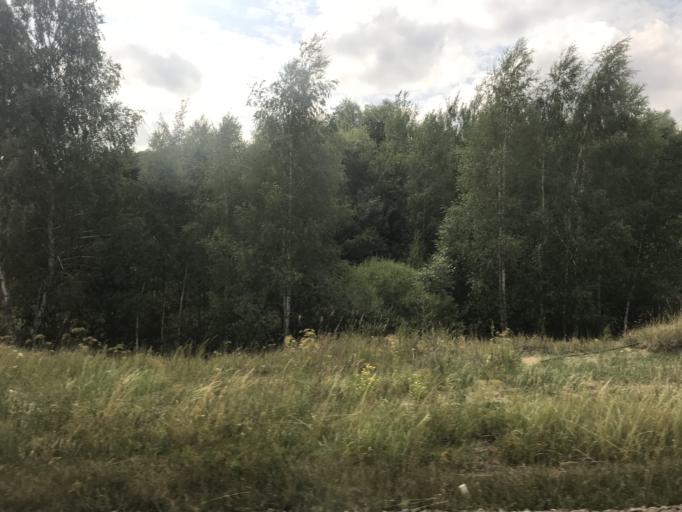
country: PL
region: Greater Poland Voivodeship
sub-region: Powiat gnieznienski
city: Lubowo
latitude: 52.5004
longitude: 17.4382
